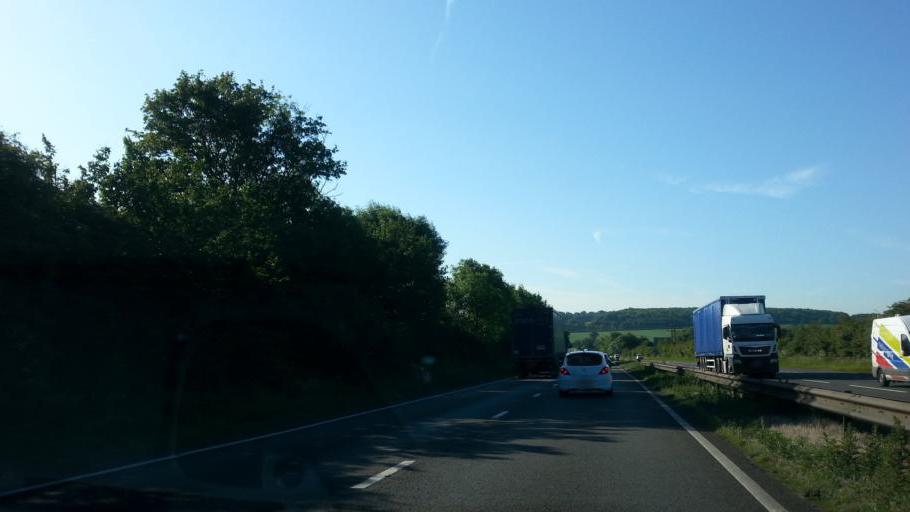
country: GB
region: England
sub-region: District of Rutland
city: Tinwell
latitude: 52.6455
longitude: -0.5039
